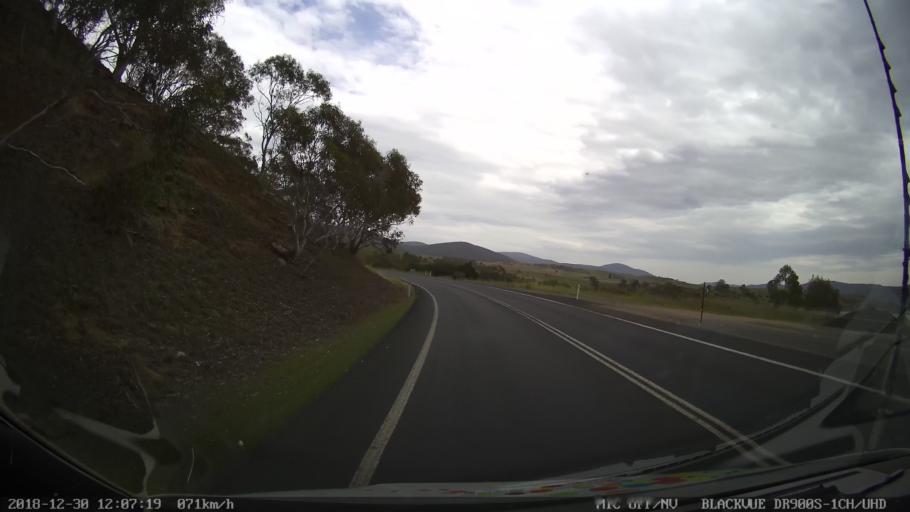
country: AU
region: New South Wales
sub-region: Snowy River
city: Jindabyne
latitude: -36.4059
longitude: 148.6003
